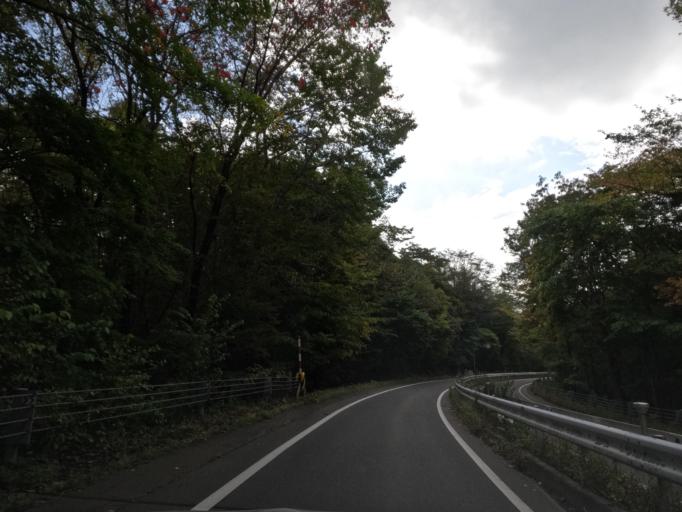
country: JP
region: Hokkaido
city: Chitose
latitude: 42.8049
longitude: 141.5844
